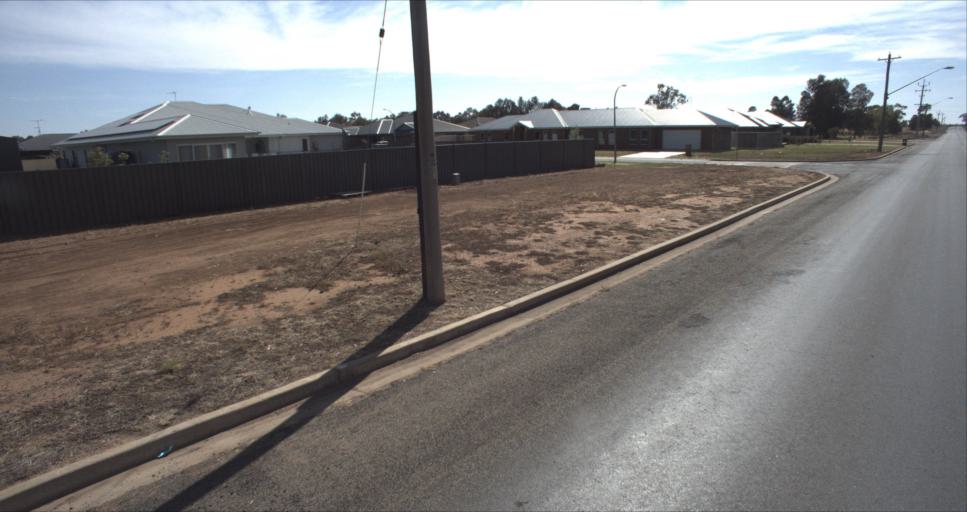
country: AU
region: New South Wales
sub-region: Leeton
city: Leeton
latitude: -34.5637
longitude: 146.4166
